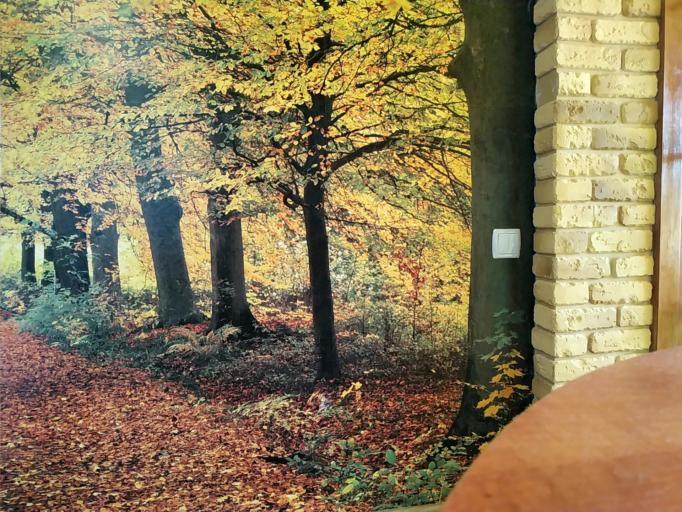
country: RU
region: Pskov
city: Dno
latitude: 57.9106
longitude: 30.1807
